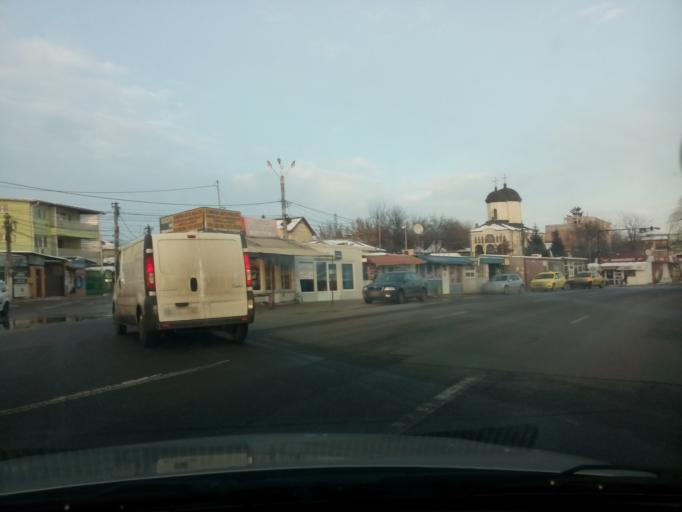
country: RO
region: Ilfov
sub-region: Comuna Pantelimon
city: Pantelimon
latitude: 44.4482
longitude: 26.2048
